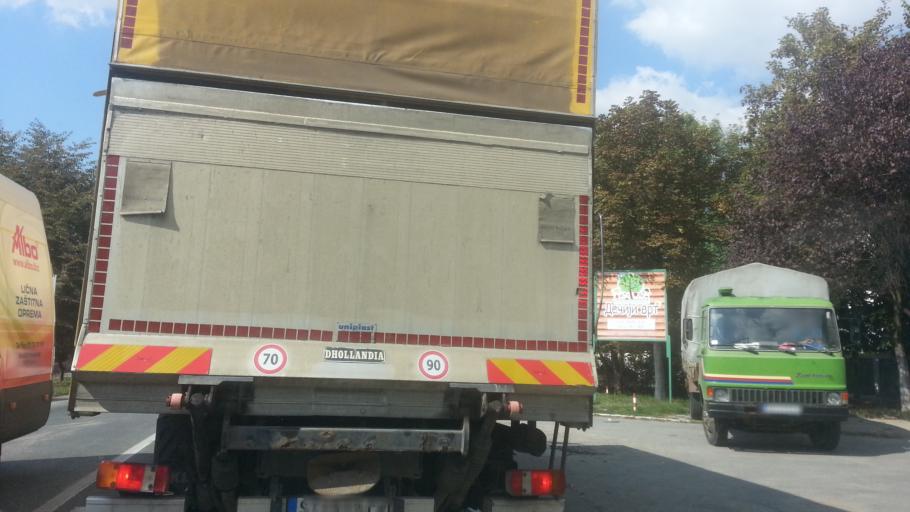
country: RS
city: Novi Banovci
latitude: 44.8969
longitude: 20.2923
